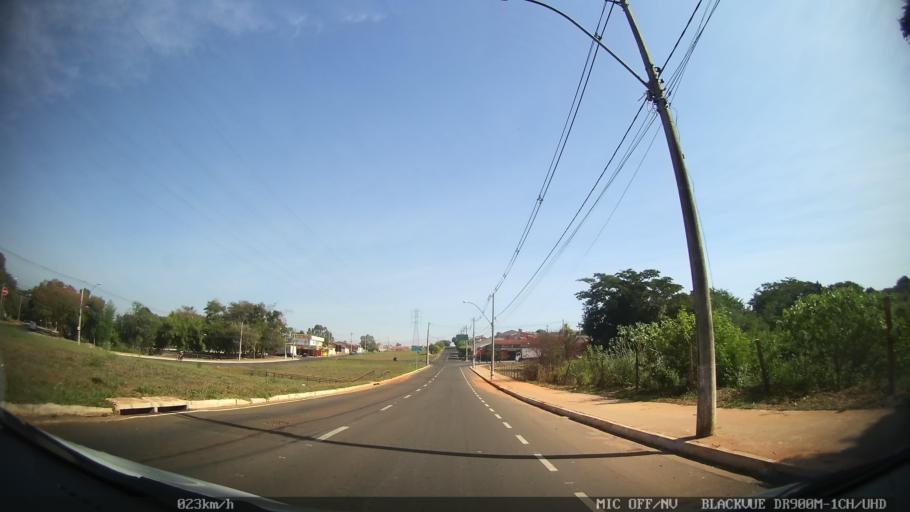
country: BR
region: Sao Paulo
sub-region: Sao Jose Do Rio Preto
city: Sao Jose do Rio Preto
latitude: -20.7932
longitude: -49.4250
